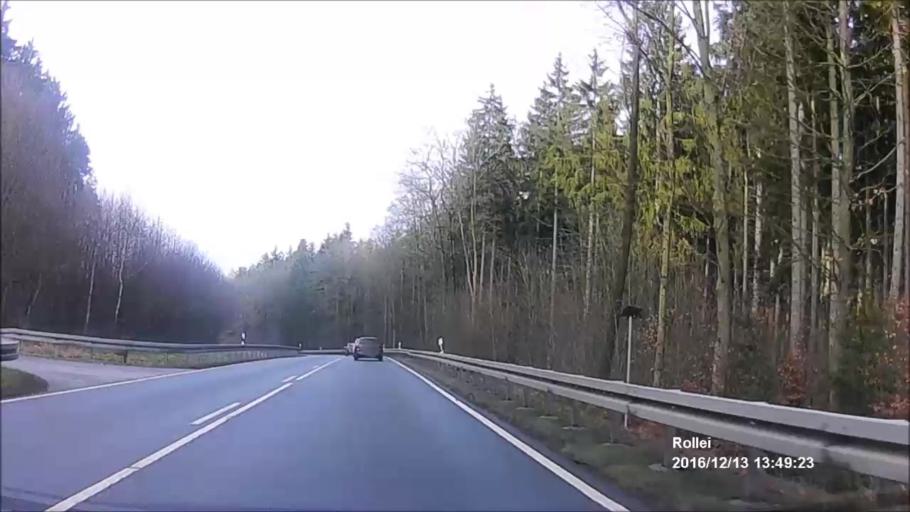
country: DE
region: Thuringia
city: Schwarza
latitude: 50.8804
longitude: 11.3264
